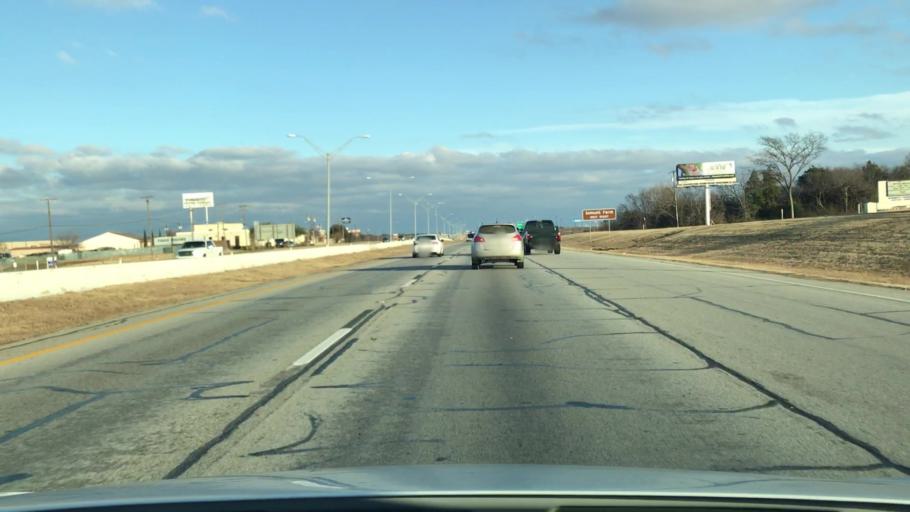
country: US
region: Texas
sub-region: Dallas County
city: Mesquite
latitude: 32.7922
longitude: -96.6047
